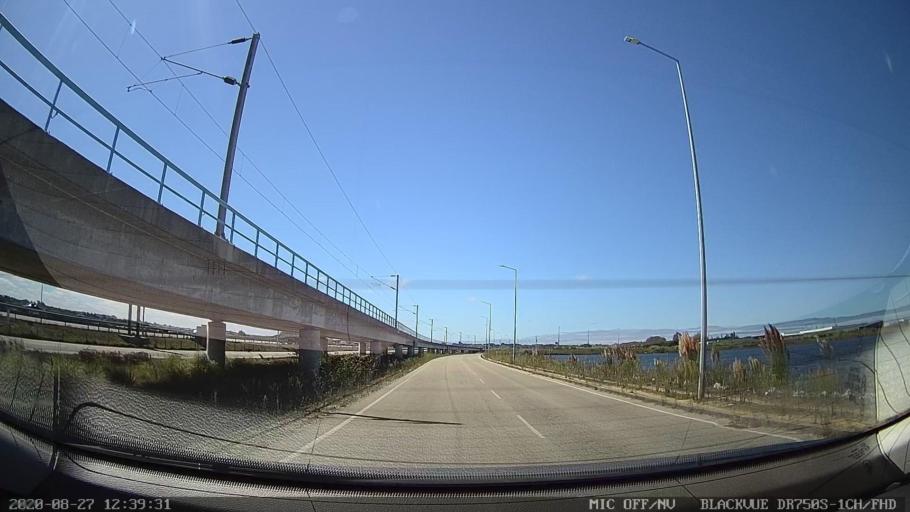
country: PT
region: Aveiro
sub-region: Aveiro
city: Aveiro
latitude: 40.6382
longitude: -8.6669
